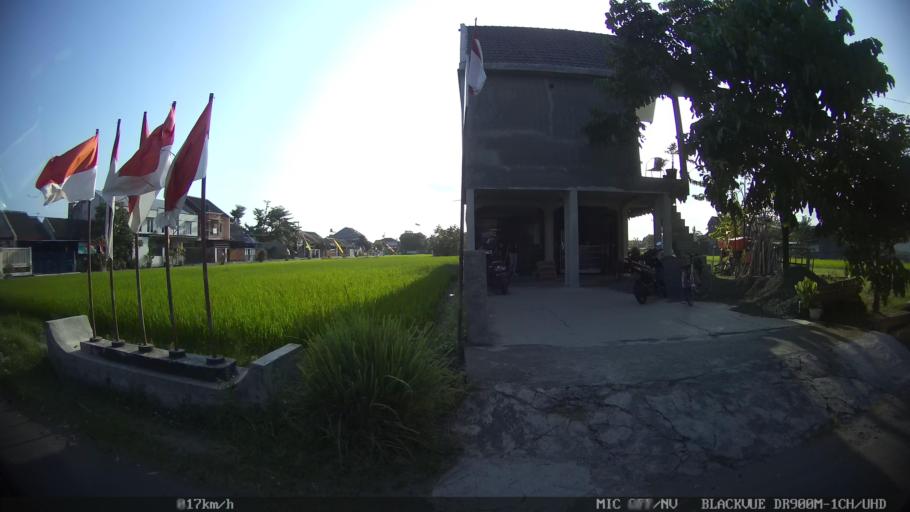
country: ID
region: Daerah Istimewa Yogyakarta
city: Gamping Lor
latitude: -7.7910
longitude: 110.3335
